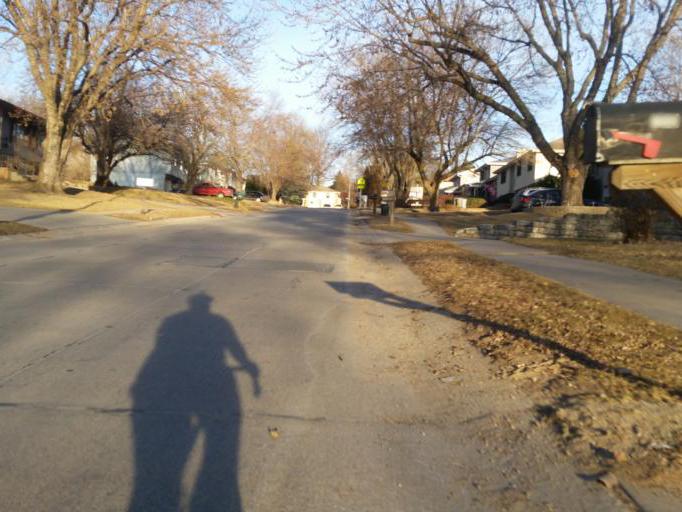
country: US
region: Nebraska
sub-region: Sarpy County
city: Offutt Air Force Base
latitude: 41.1331
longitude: -95.9703
